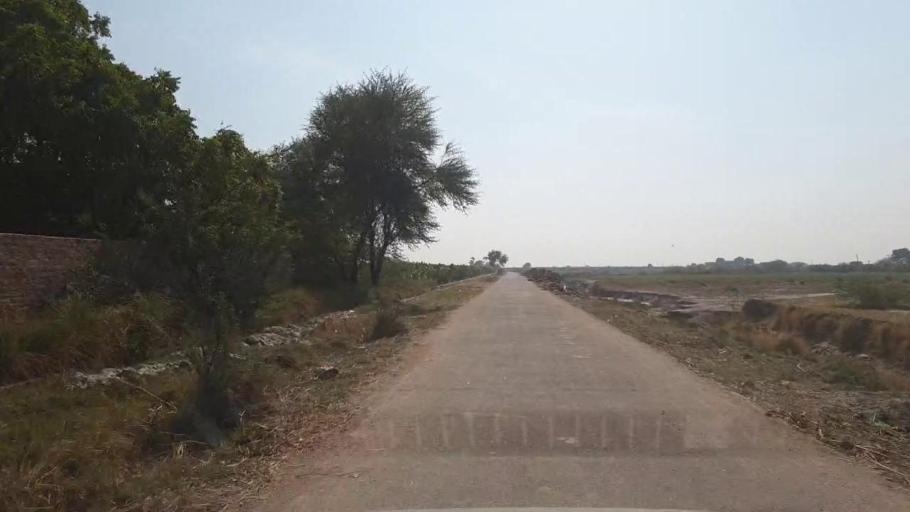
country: PK
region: Sindh
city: Chambar
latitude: 25.3611
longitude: 68.8218
